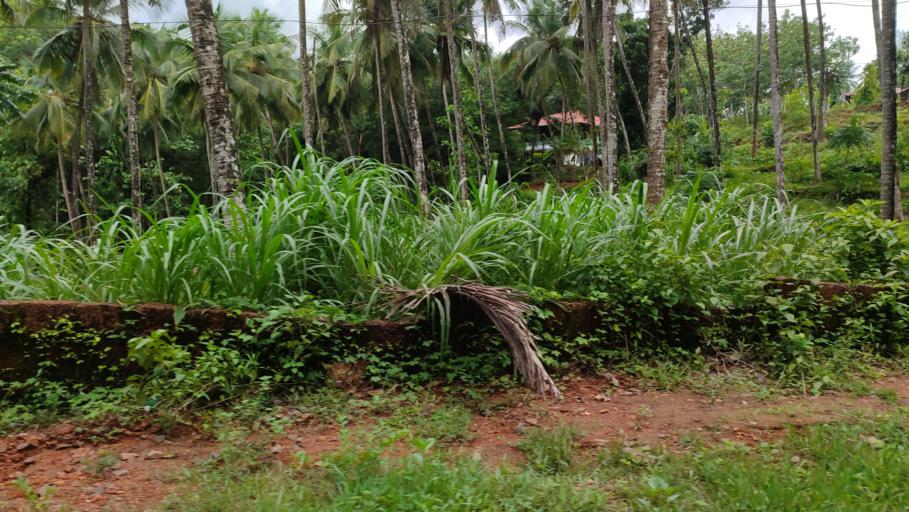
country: IN
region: Kerala
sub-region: Kasaragod District
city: Nileshwar
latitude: 12.2996
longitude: 75.2961
